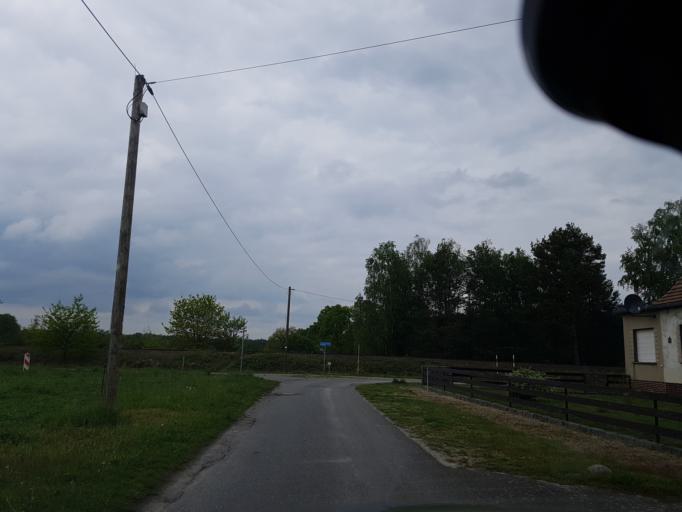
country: DE
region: Brandenburg
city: Crinitz
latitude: 51.7406
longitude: 13.7630
